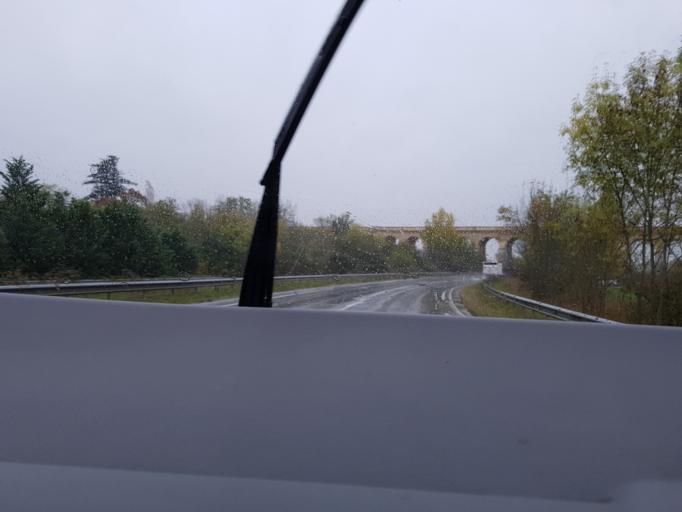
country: FR
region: Aquitaine
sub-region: Departement de la Gironde
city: Saint-Vincent-de-Paul
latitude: 44.9607
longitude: -0.4679
